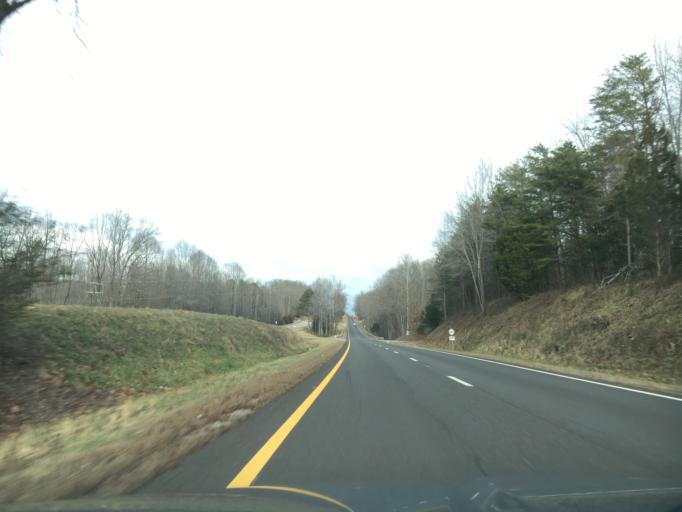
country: US
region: Virginia
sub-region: Lunenburg County
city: Victoria
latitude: 37.1248
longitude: -78.3272
